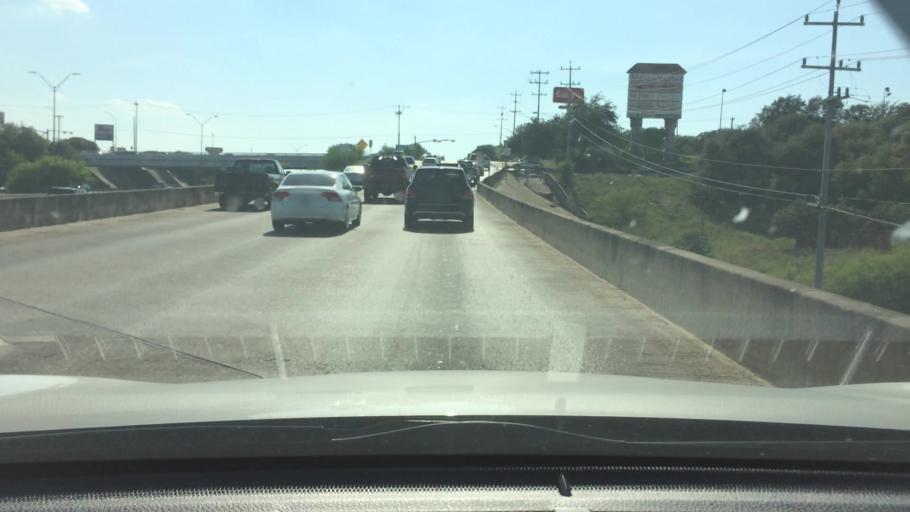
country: US
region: Texas
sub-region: Bexar County
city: Hollywood Park
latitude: 29.6091
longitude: -98.5061
